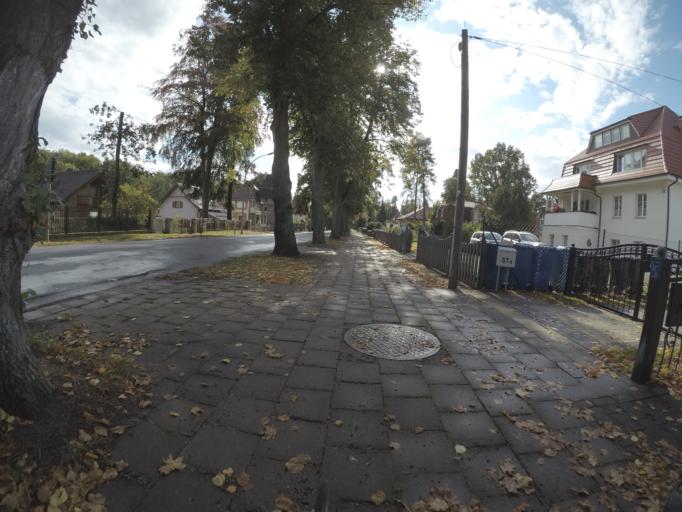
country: DE
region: Brandenburg
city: Strausberg
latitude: 52.5433
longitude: 13.8564
